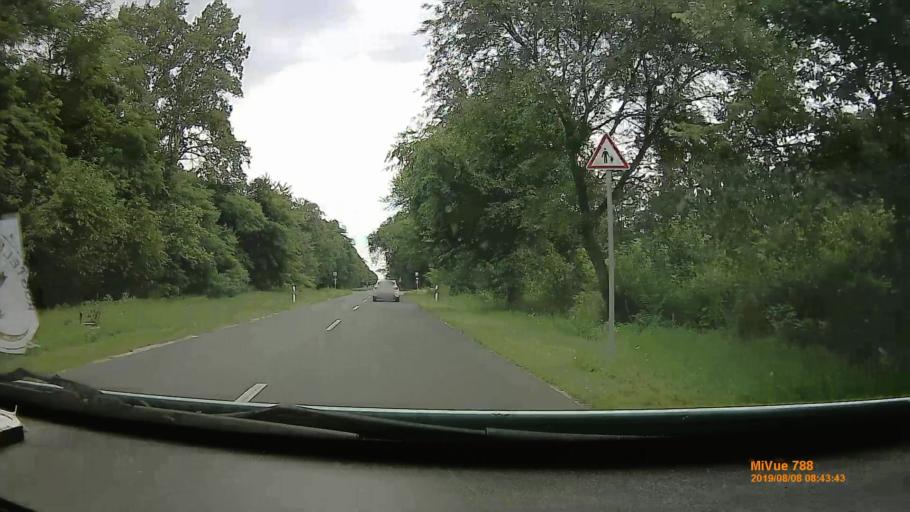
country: HU
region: Hajdu-Bihar
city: Debrecen
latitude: 47.5857
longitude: 21.6307
